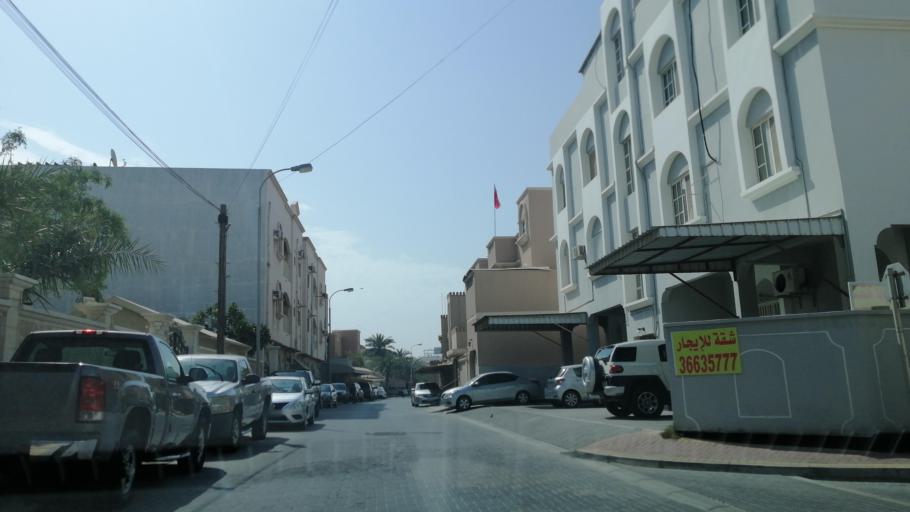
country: BH
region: Muharraq
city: Al Hadd
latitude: 26.2485
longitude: 50.6528
